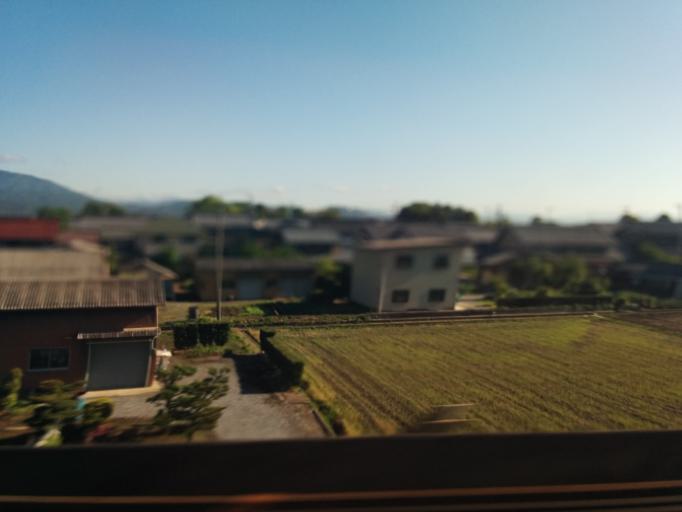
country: JP
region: Gifu
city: Tarui
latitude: 35.3499
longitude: 136.5604
